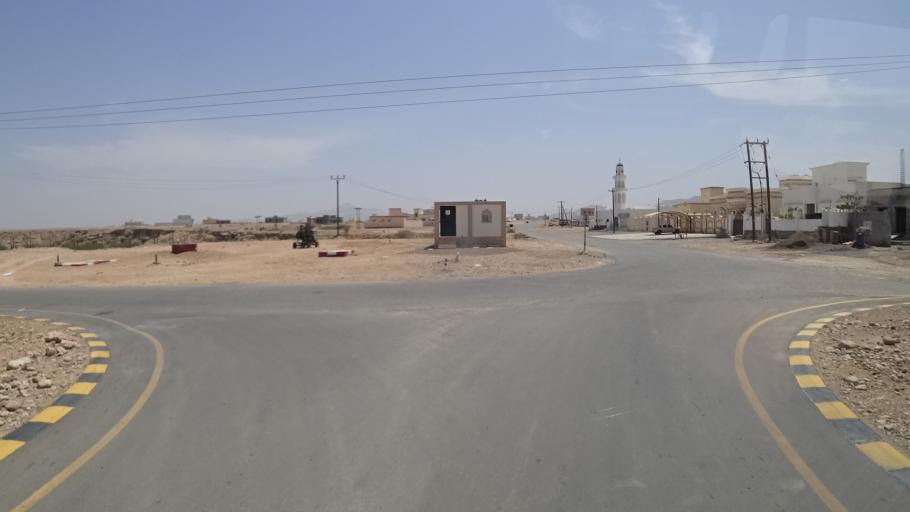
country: OM
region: Ash Sharqiyah
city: Sur
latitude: 22.6043
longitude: 59.4659
